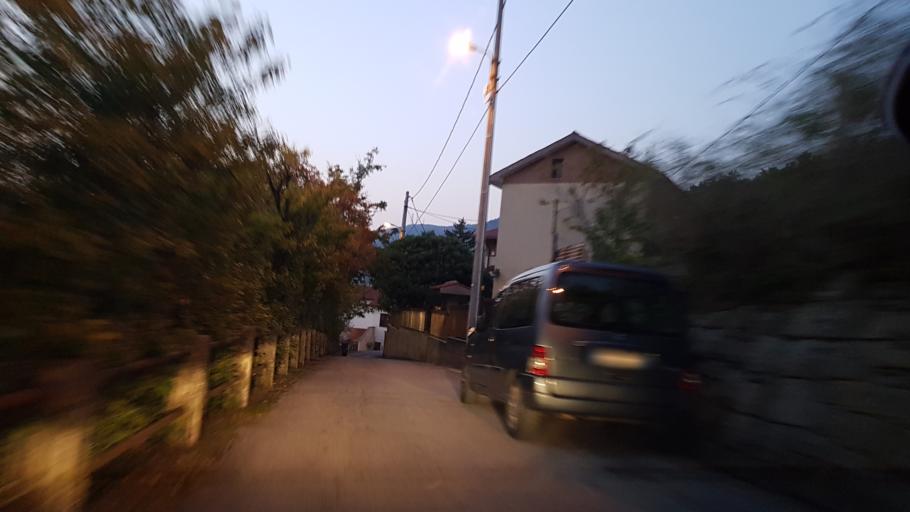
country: IT
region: Friuli Venezia Giulia
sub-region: Provincia di Trieste
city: Trieste
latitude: 45.6502
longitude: 13.8173
